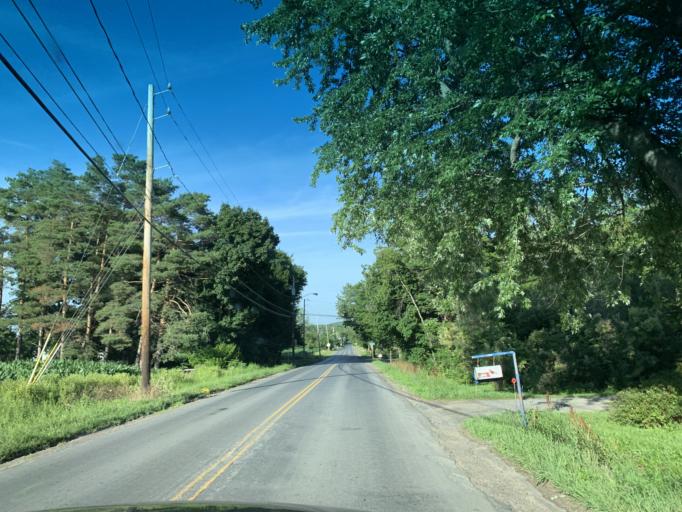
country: US
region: New York
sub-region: Oneida County
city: Vernon
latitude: 43.0527
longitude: -75.4991
